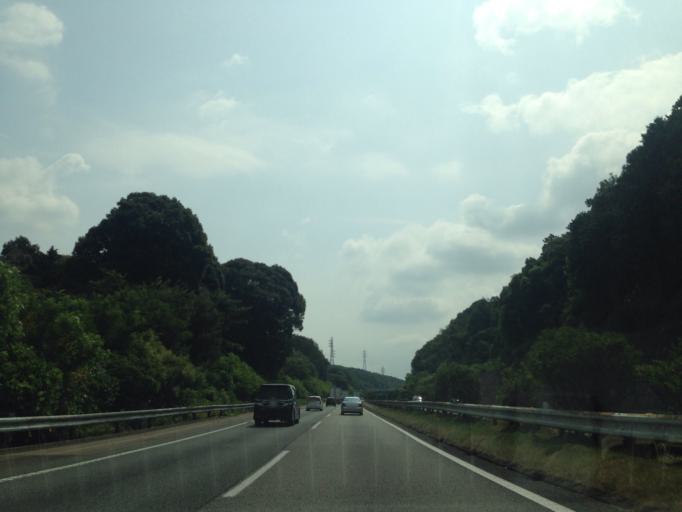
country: JP
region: Aichi
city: Kozakai-cho
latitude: 34.8621
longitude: 137.3171
